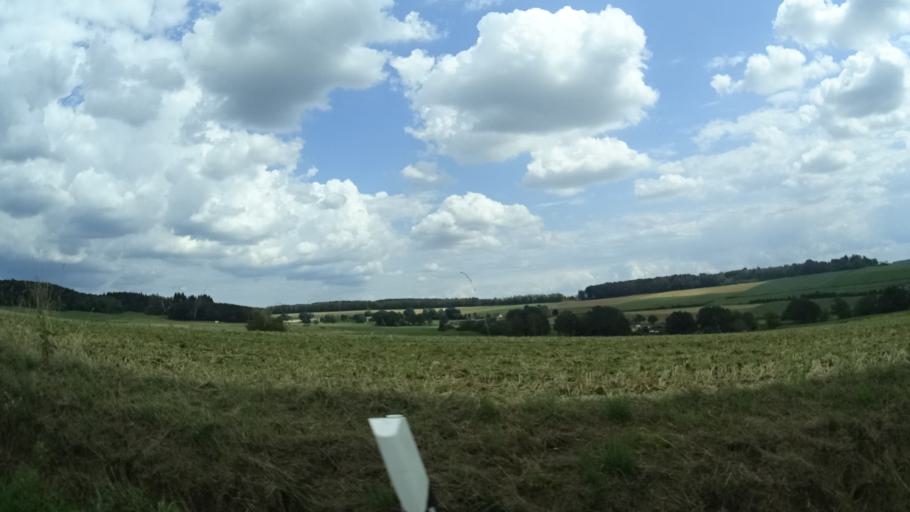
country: DE
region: Hesse
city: Gedern
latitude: 50.3916
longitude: 9.1982
